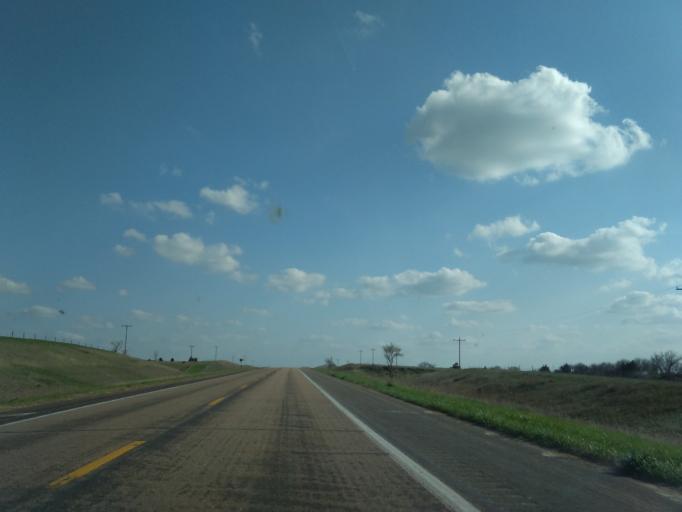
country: US
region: Nebraska
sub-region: Webster County
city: Red Cloud
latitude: 40.1312
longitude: -98.5190
